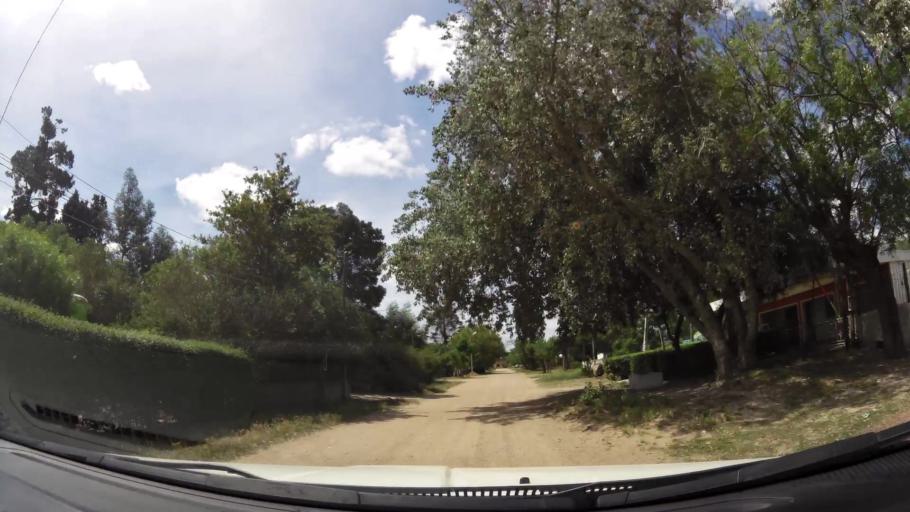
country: UY
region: San Jose
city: Delta del Tigre
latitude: -34.7509
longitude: -56.4578
